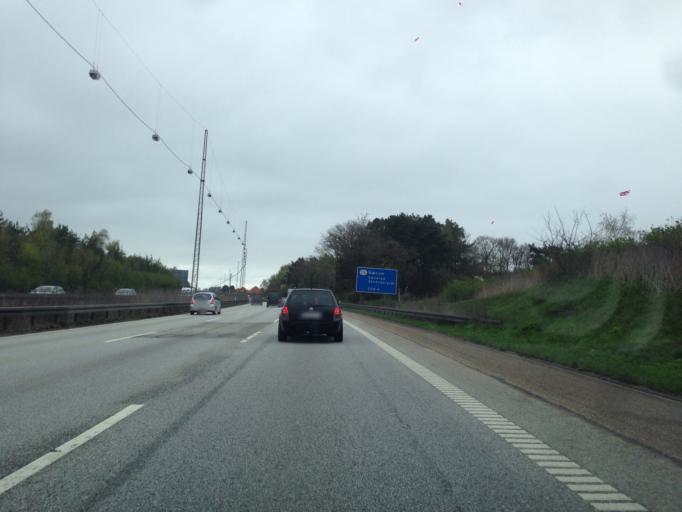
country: DK
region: Capital Region
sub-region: Rudersdal Kommune
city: Trorod
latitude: 55.8059
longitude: 12.5331
